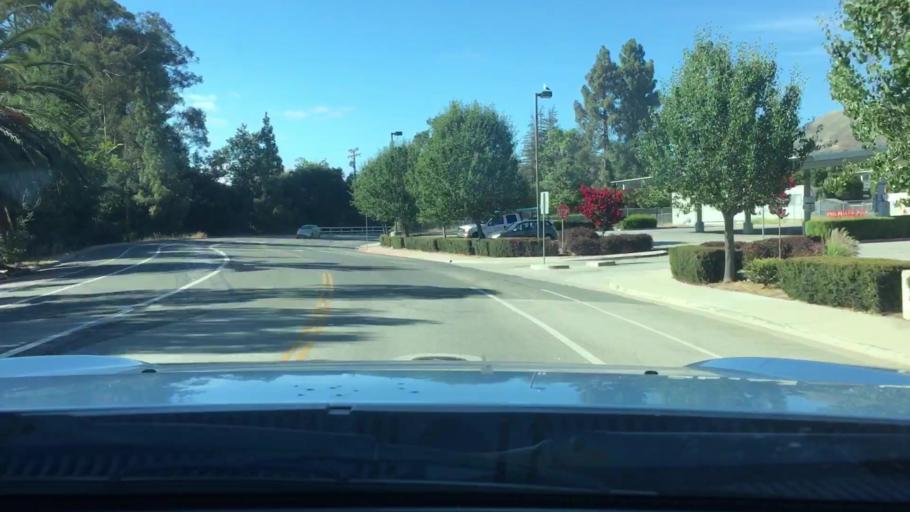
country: US
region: California
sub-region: San Luis Obispo County
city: San Luis Obispo
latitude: 35.2825
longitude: -120.6527
